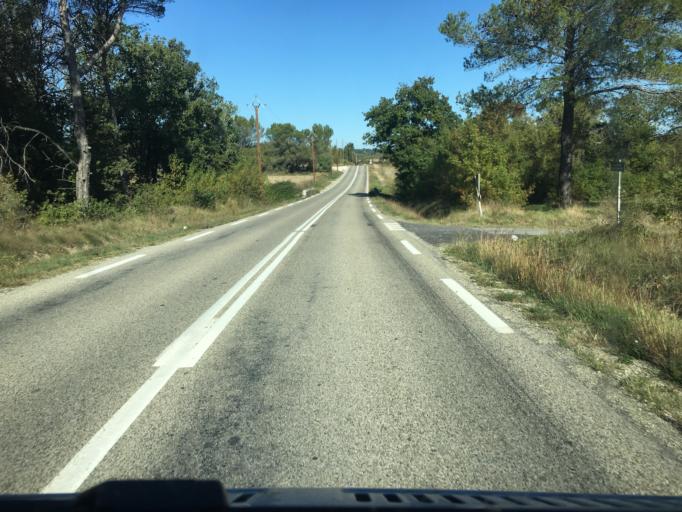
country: FR
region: Languedoc-Roussillon
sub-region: Departement du Gard
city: Ledignan
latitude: 43.9632
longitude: 4.0982
